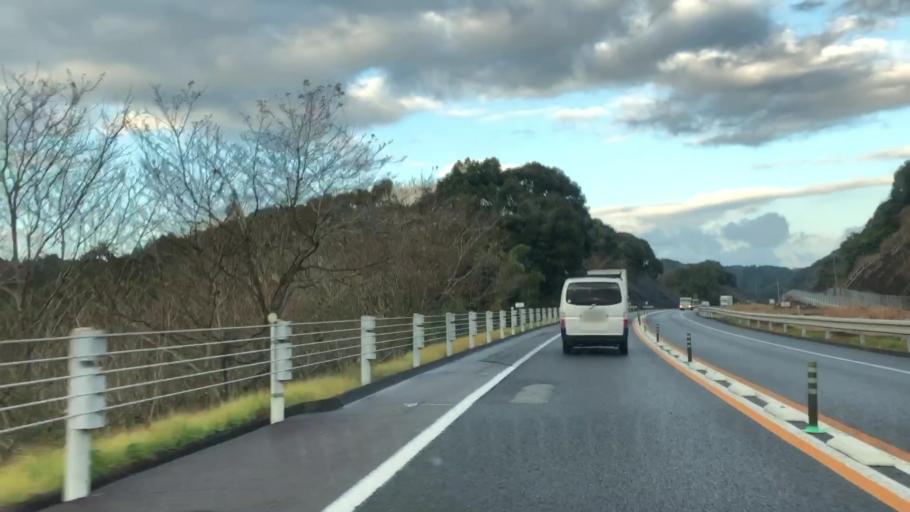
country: JP
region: Saga Prefecture
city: Ureshinomachi-shimojuku
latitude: 33.1439
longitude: 129.9539
